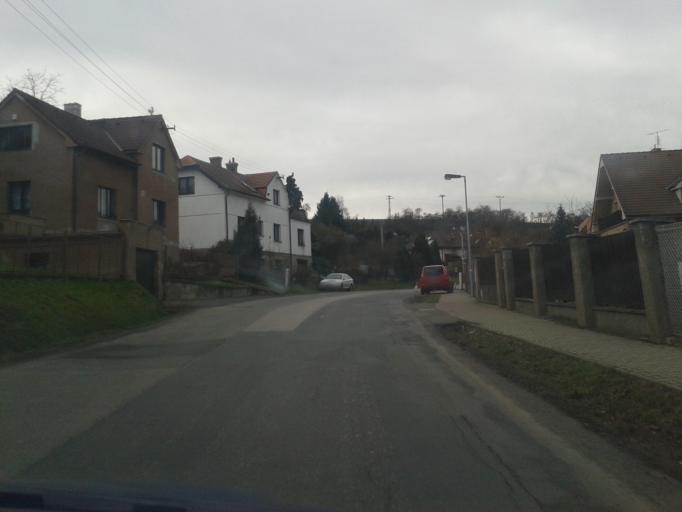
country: CZ
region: Central Bohemia
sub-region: Okres Beroun
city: Kraluv Dvur
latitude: 49.9489
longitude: 14.0292
